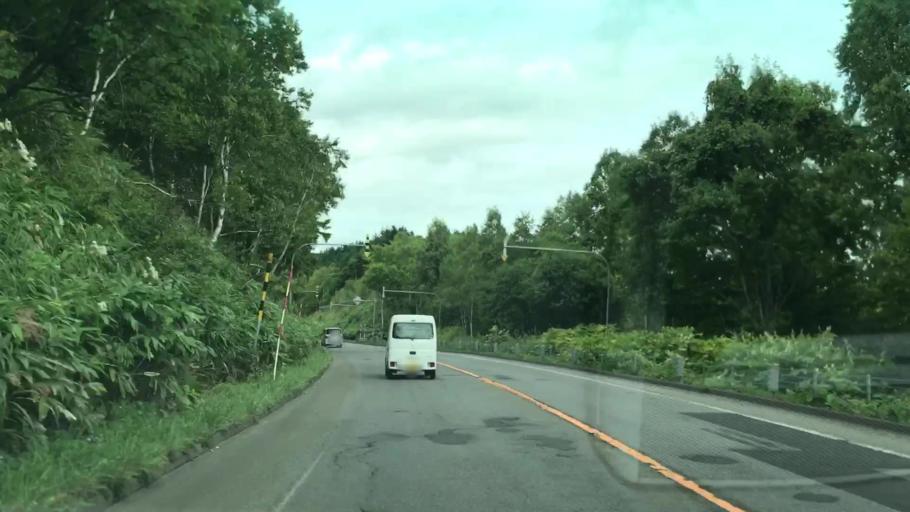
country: JP
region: Hokkaido
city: Niseko Town
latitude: 42.9295
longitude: 140.7141
